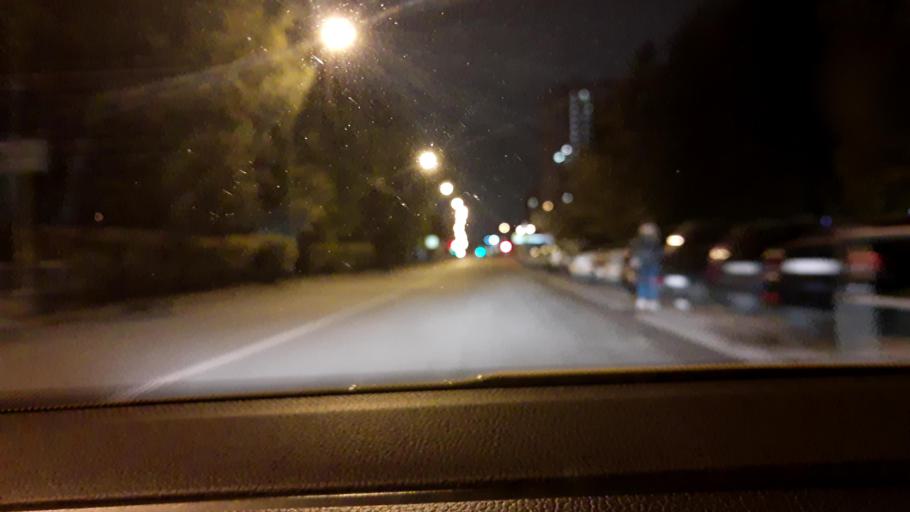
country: RU
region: Moskovskaya
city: Dolgoprudnyy
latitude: 55.9407
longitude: 37.5098
